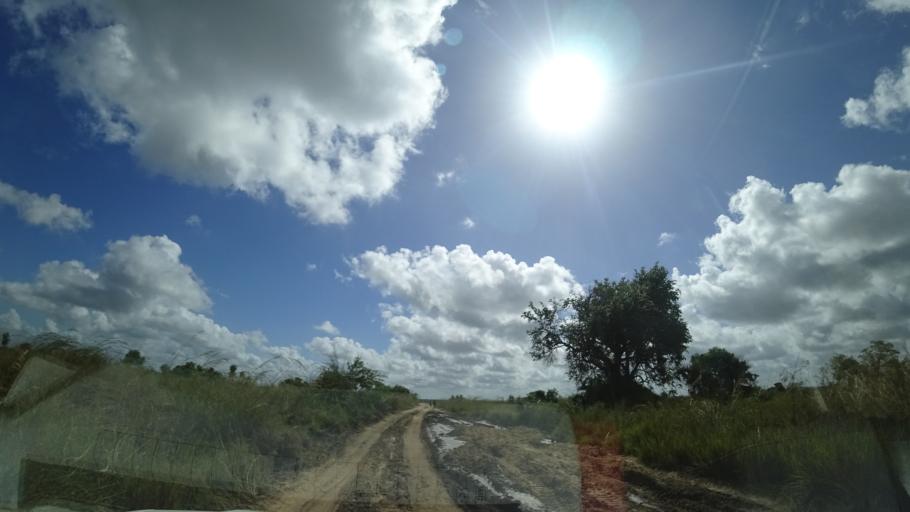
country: MZ
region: Sofala
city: Dondo
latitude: -19.4034
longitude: 34.5672
